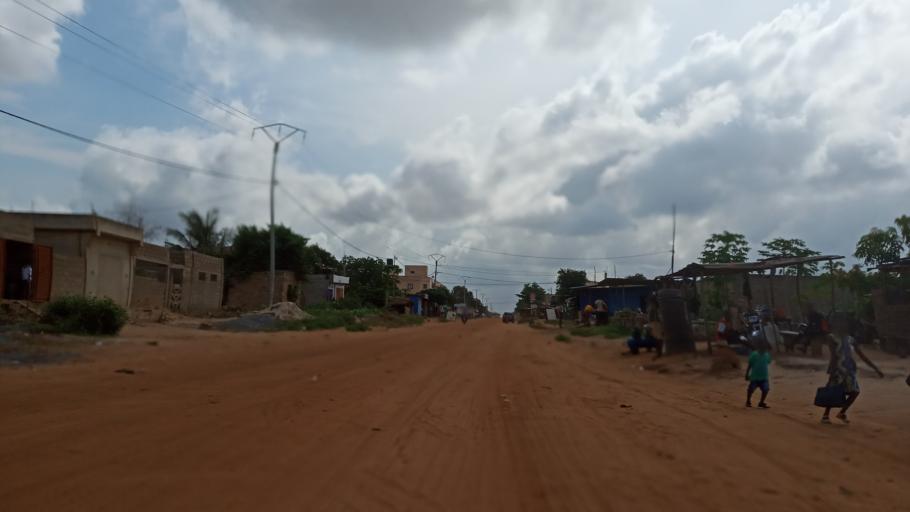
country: TG
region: Maritime
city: Lome
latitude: 6.2334
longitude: 1.1436
